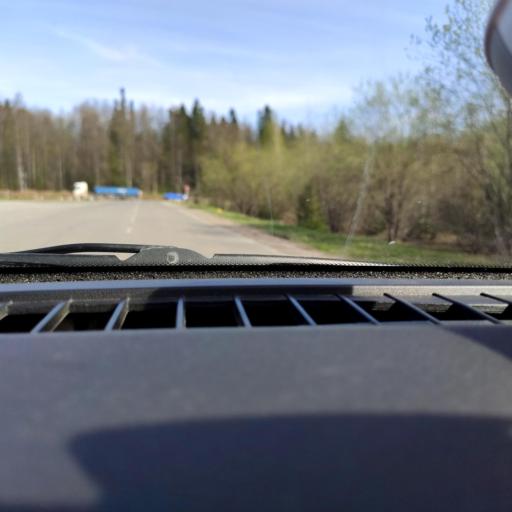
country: RU
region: Perm
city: Perm
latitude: 58.2475
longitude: 56.1559
